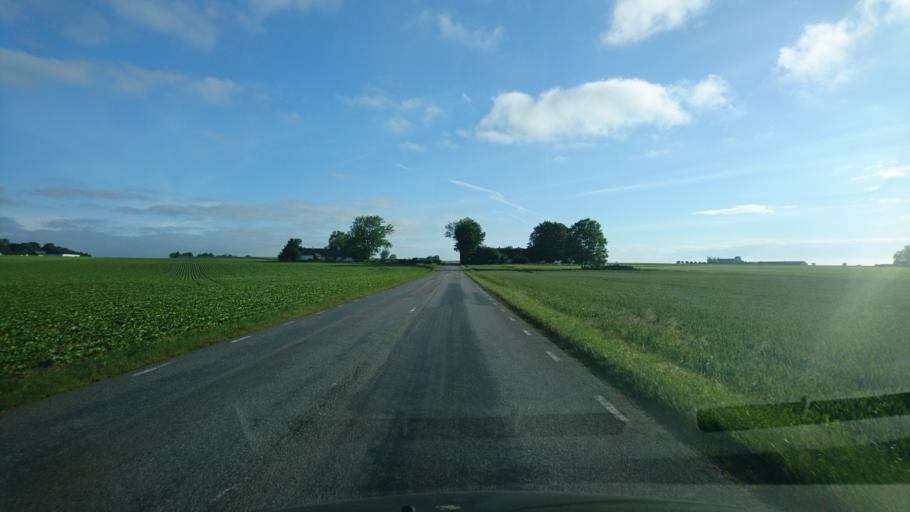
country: SE
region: Skane
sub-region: Tomelilla Kommun
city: Tomelilla
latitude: 55.4770
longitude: 14.0997
